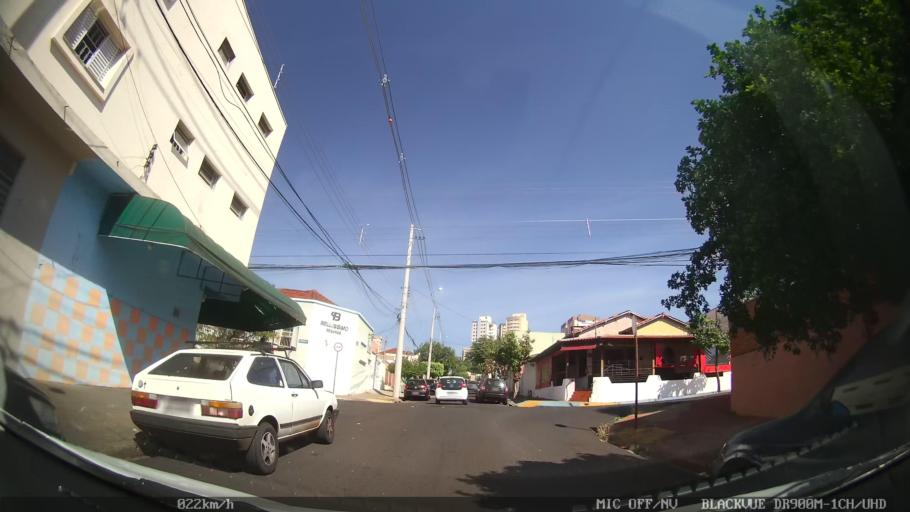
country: BR
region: Sao Paulo
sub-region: Ribeirao Preto
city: Ribeirao Preto
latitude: -21.1829
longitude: -47.8003
